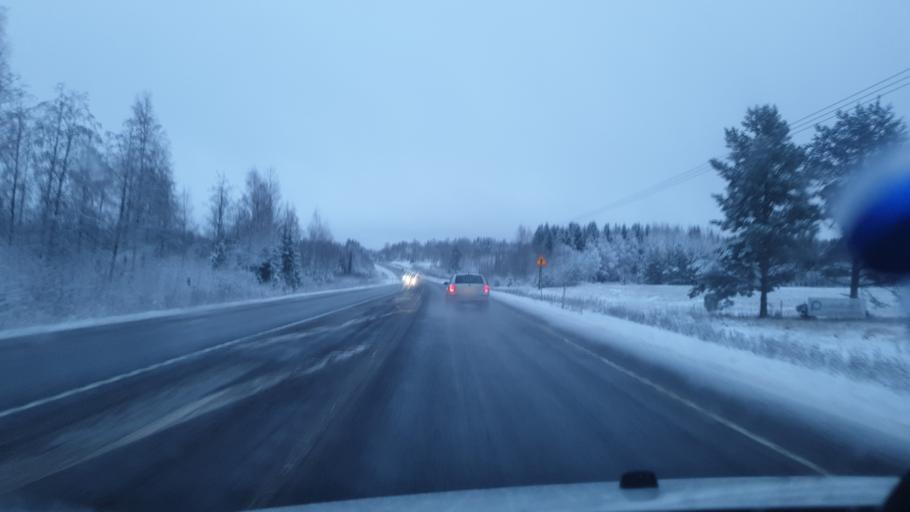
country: FI
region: Central Finland
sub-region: Saarijaervi-Viitasaari
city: Viitasaari
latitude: 63.1171
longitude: 25.7945
